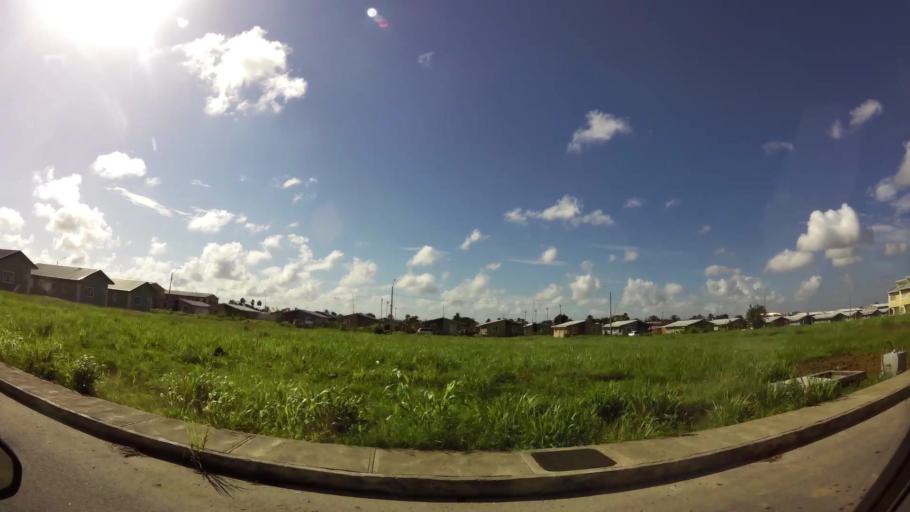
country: TT
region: Chaguanas
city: Chaguanas
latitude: 10.5311
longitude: -61.3933
